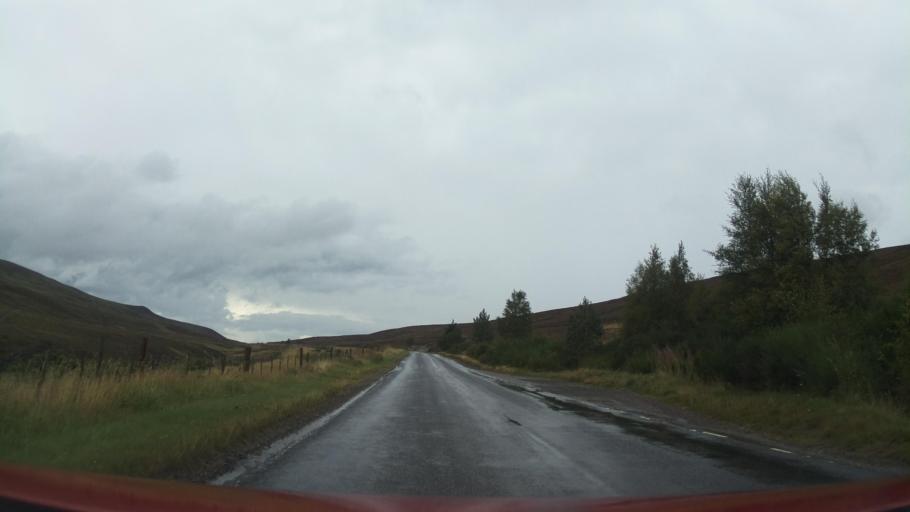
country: GB
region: Scotland
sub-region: Highland
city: Grantown on Spey
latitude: 57.2633
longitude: -3.4929
